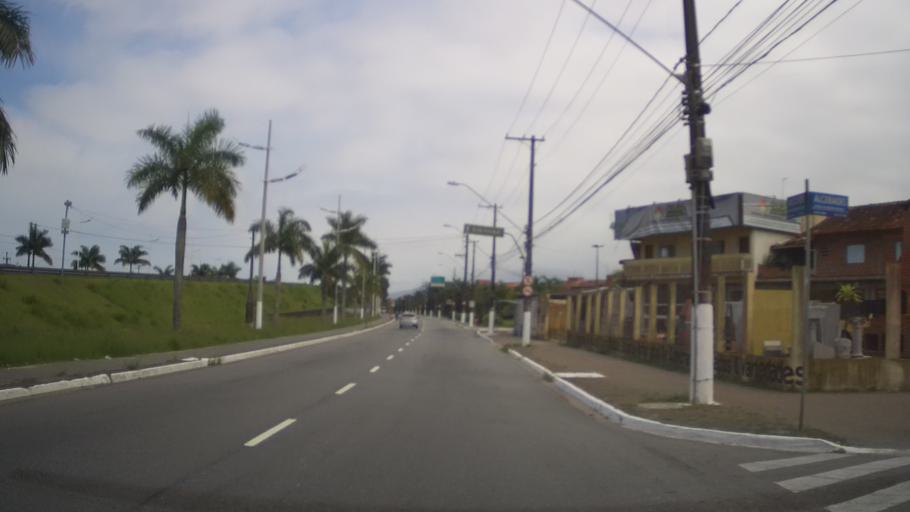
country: BR
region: Sao Paulo
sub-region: Praia Grande
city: Praia Grande
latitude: -24.0261
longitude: -46.4963
